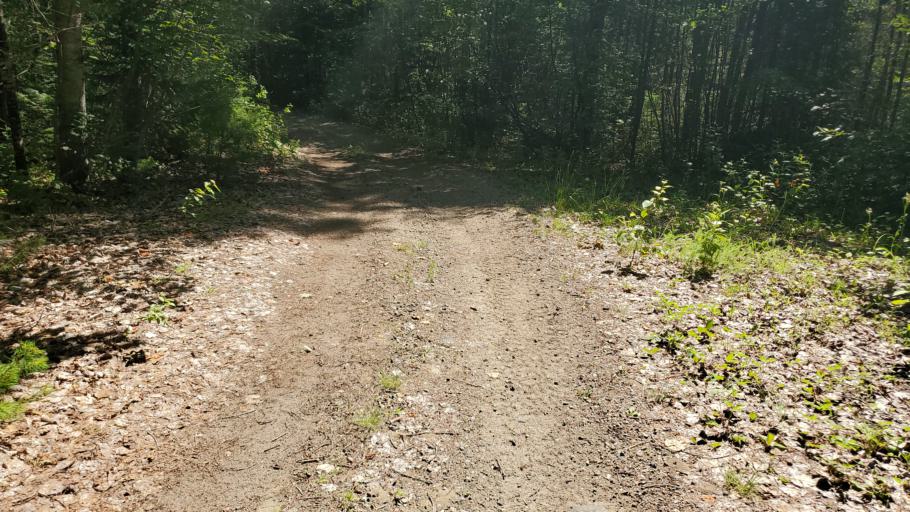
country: CA
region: Ontario
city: Mattawa
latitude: 46.2607
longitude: -78.2747
